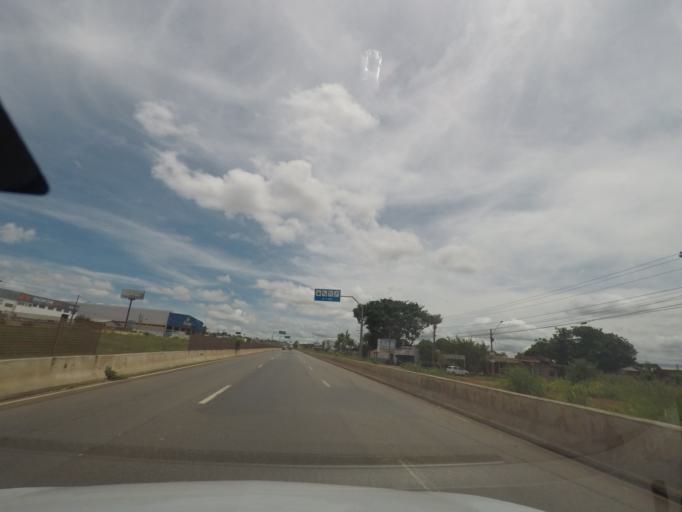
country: BR
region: Goias
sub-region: Goiania
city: Goiania
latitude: -16.7147
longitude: -49.3617
